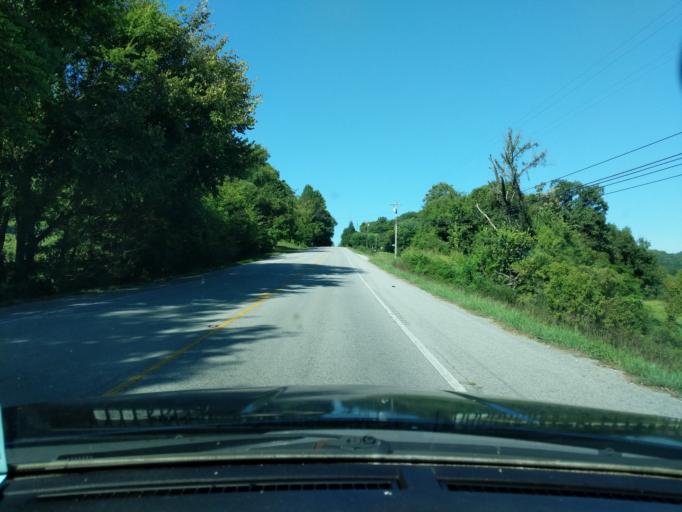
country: US
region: Tennessee
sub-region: Smith County
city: Carthage
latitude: 36.2565
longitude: -85.9926
